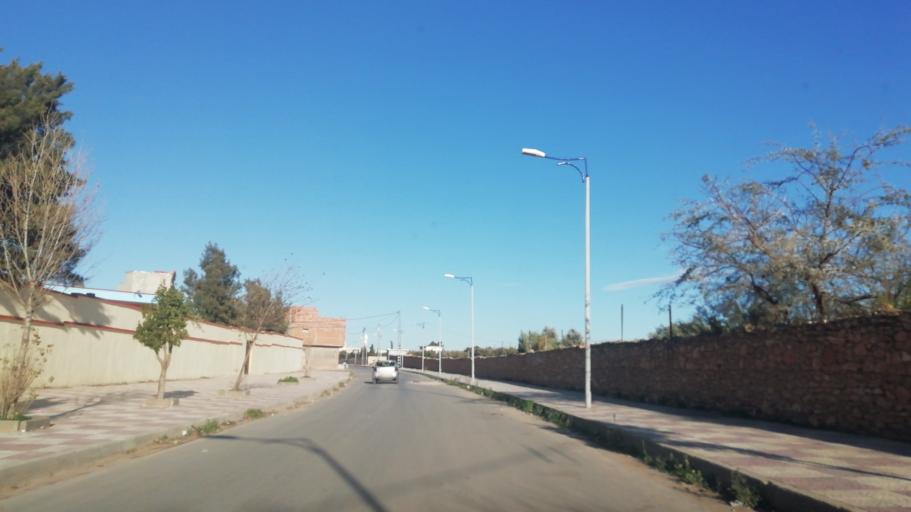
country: DZ
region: Oran
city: Sidi ech Chahmi
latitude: 35.6898
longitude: -0.4955
